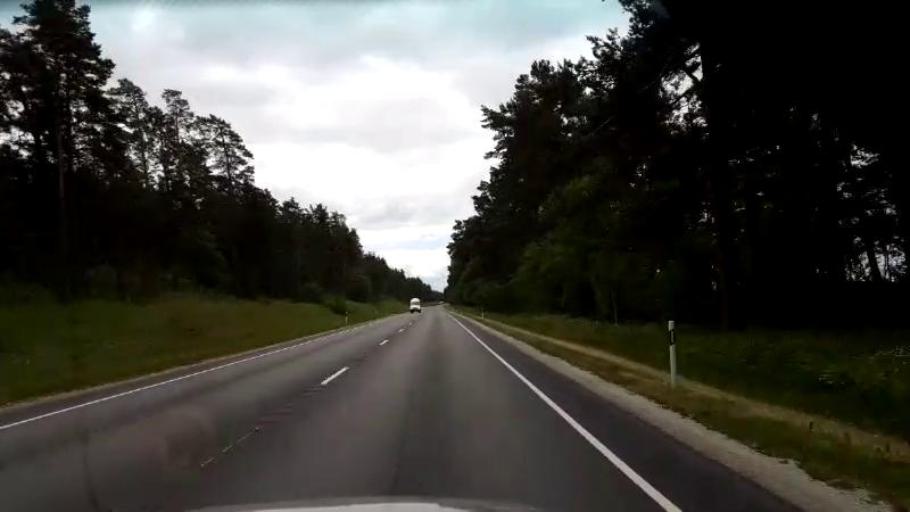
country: EE
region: Paernumaa
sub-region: Paernu linn
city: Parnu
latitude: 58.1706
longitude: 24.4954
